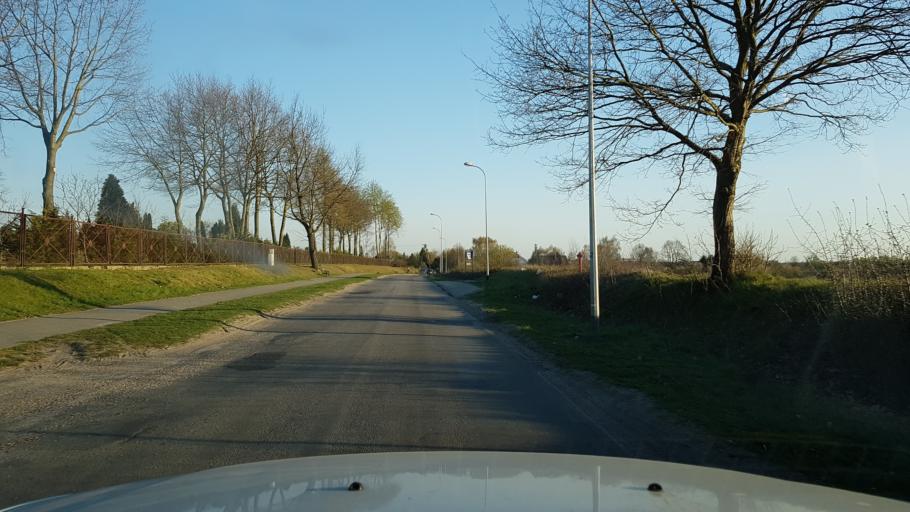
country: PL
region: West Pomeranian Voivodeship
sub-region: Powiat bialogardzki
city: Bialogard
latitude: 54.0228
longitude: 15.9877
